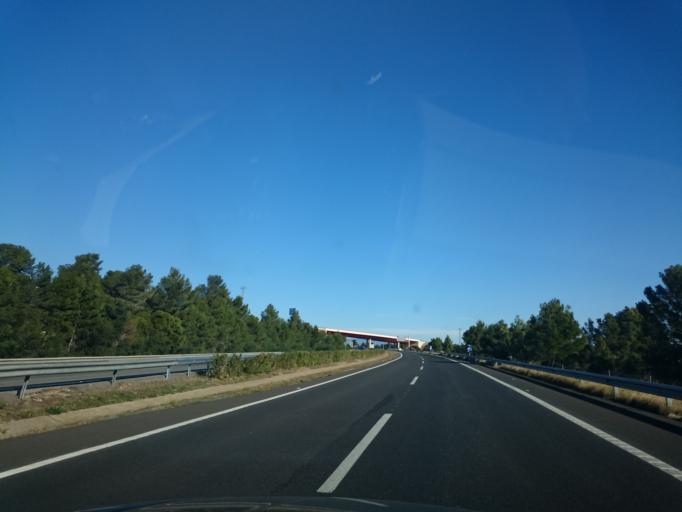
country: ES
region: Catalonia
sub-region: Provincia de Tarragona
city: Colldejou
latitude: 40.9953
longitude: 0.9071
